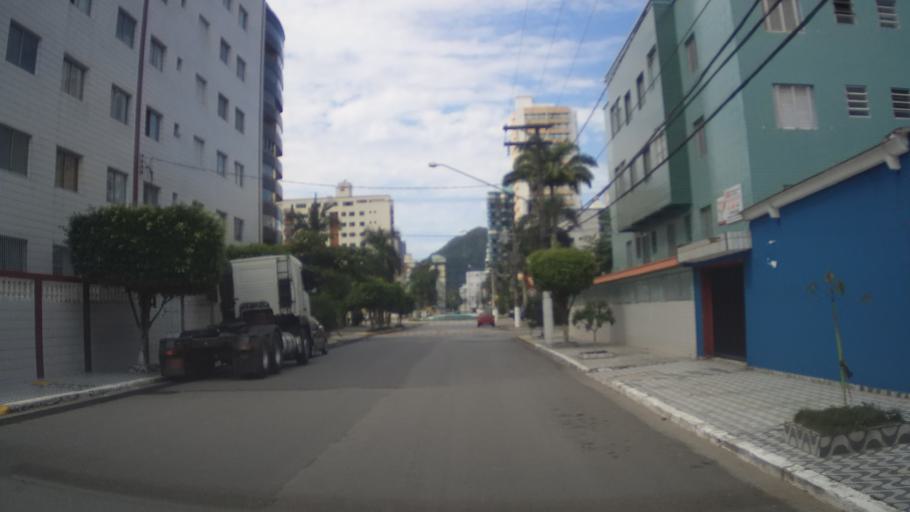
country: BR
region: Sao Paulo
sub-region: Praia Grande
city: Praia Grande
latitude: -24.0110
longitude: -46.4226
